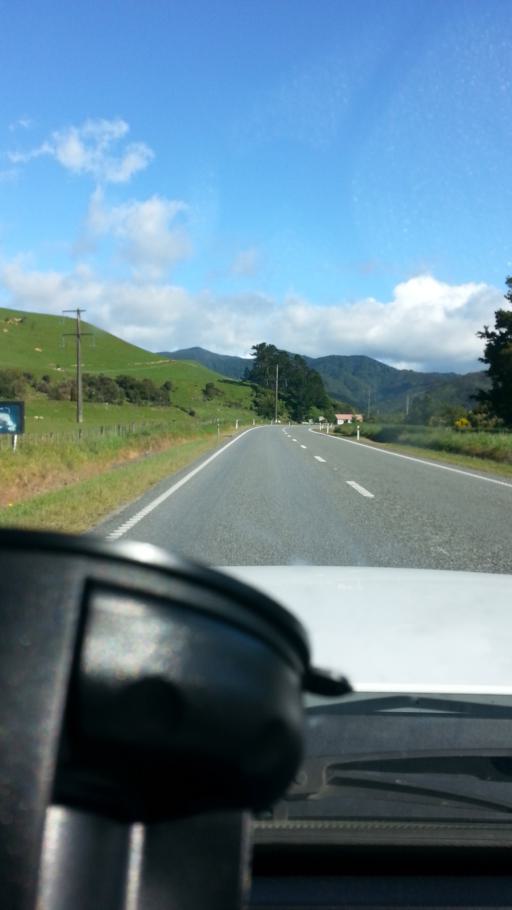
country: NZ
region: Wellington
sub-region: Masterton District
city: Masterton
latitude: -40.7723
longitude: 175.6111
